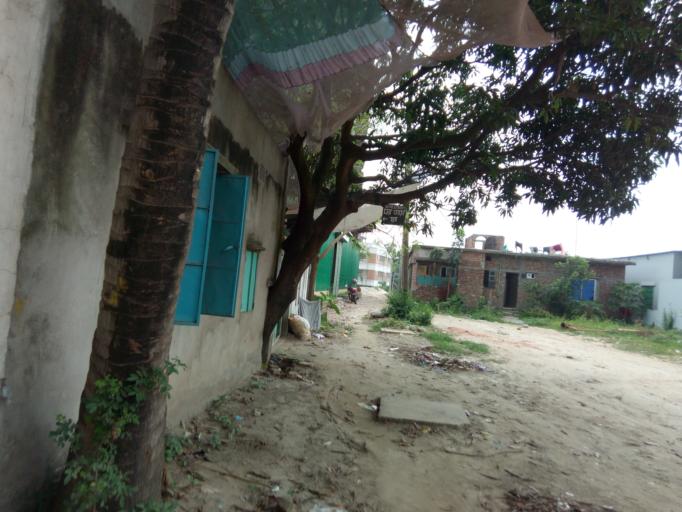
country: BD
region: Dhaka
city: Paltan
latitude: 23.7543
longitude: 90.4539
